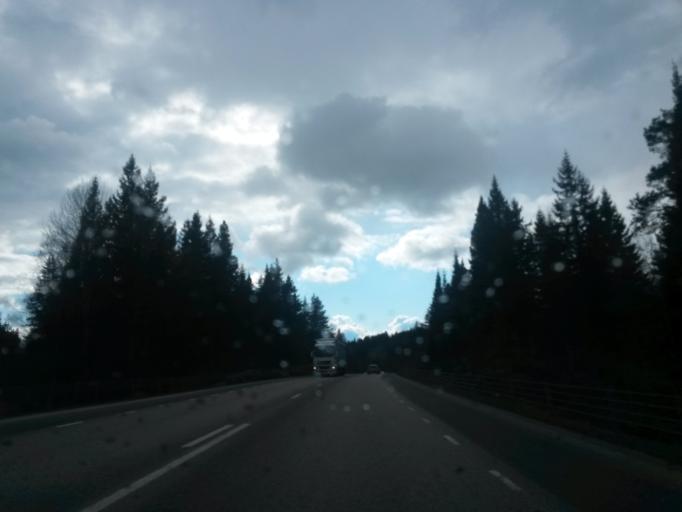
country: SE
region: Vaestra Goetaland
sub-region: Skovde Kommun
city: Skultorp
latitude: 58.3860
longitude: 13.7428
